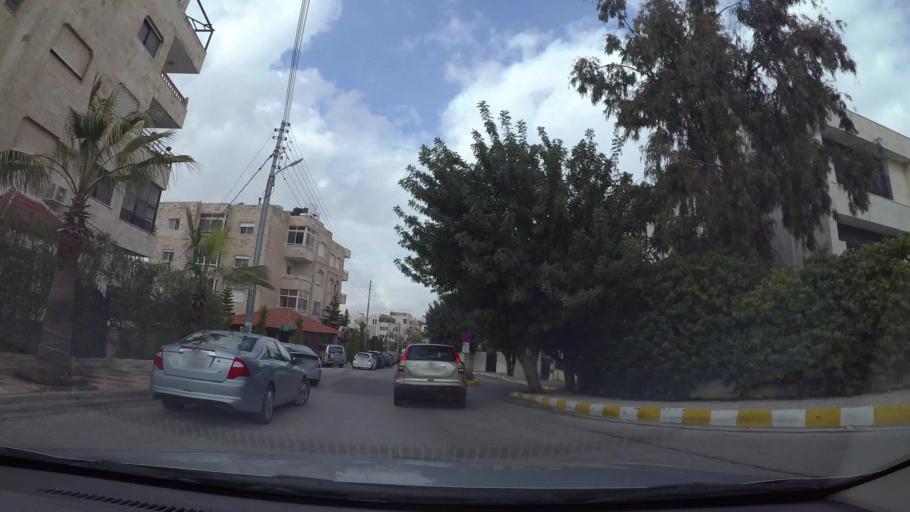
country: JO
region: Amman
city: Al Jubayhah
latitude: 31.9865
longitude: 35.8463
